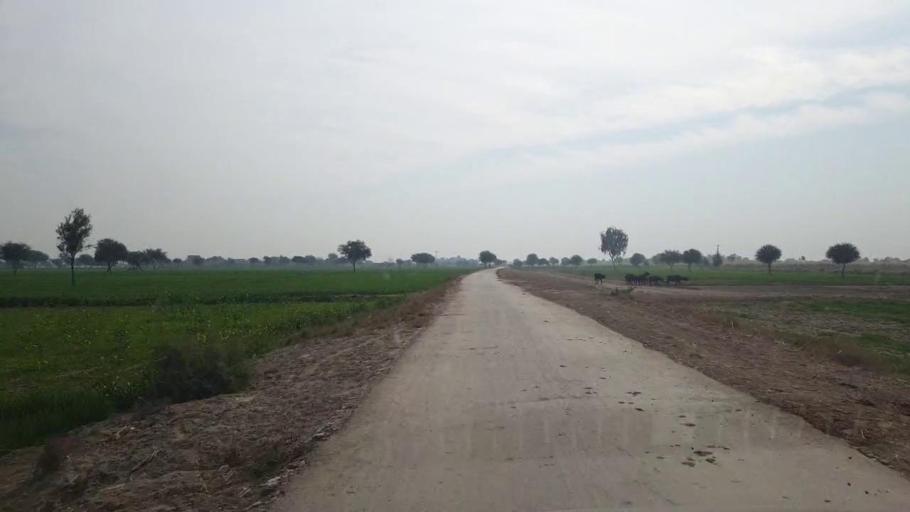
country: PK
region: Sindh
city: Shahdadpur
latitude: 25.9529
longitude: 68.6994
